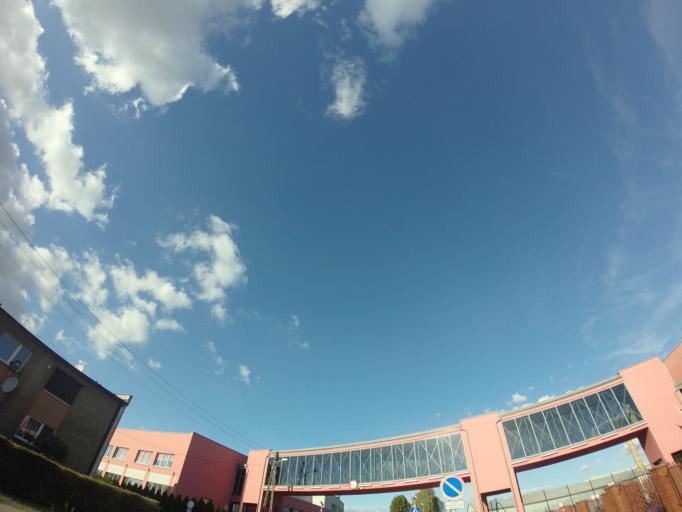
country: PL
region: Greater Poland Voivodeship
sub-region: Powiat grodziski
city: Rakoniewice
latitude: 52.1417
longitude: 16.2734
